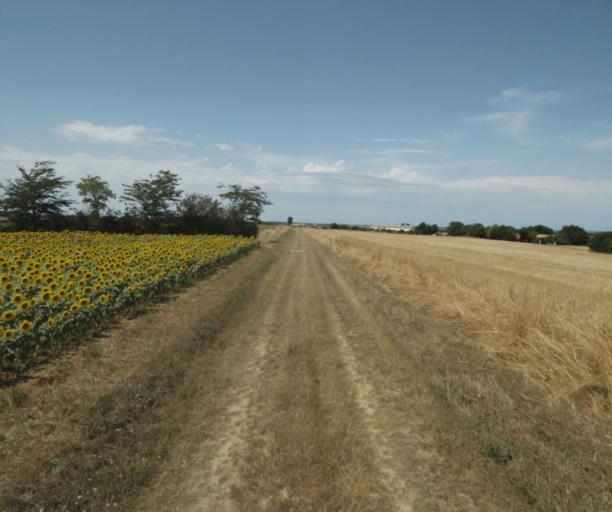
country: FR
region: Midi-Pyrenees
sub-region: Departement de la Haute-Garonne
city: Saint-Felix-Lauragais
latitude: 43.4509
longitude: 1.8571
